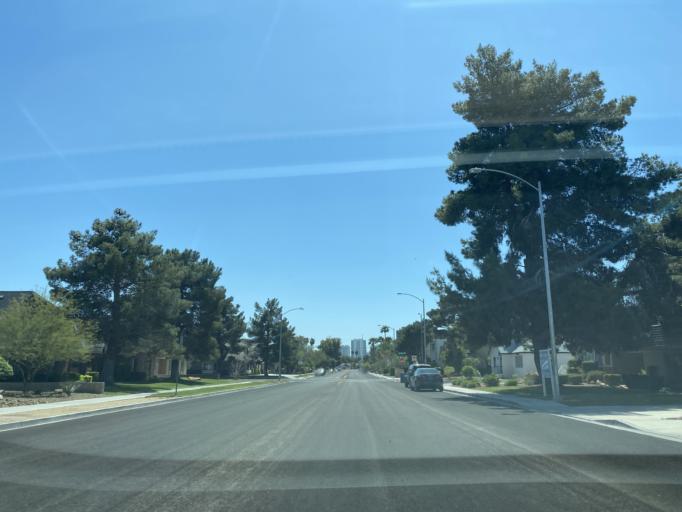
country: US
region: Nevada
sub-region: Clark County
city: Las Vegas
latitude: 36.1622
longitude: -115.1395
